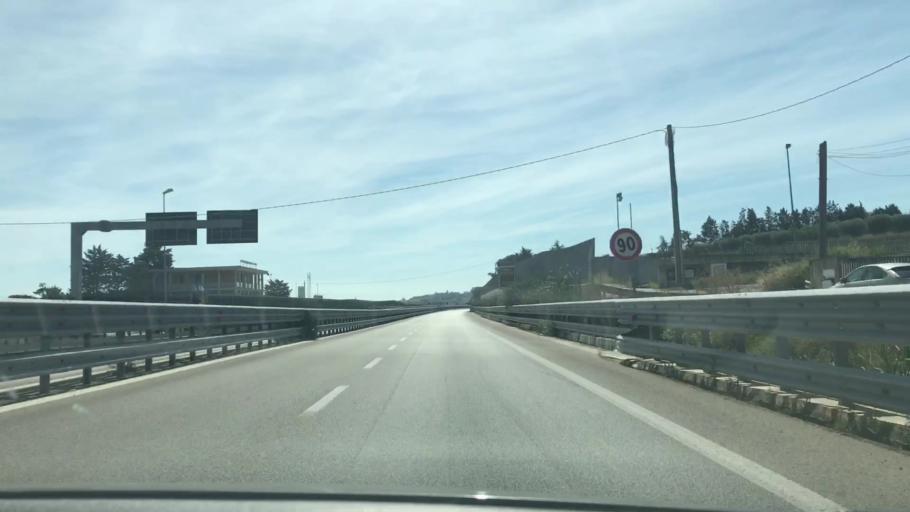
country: IT
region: Basilicate
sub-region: Provincia di Matera
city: Matera
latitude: 40.6978
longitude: 16.5895
